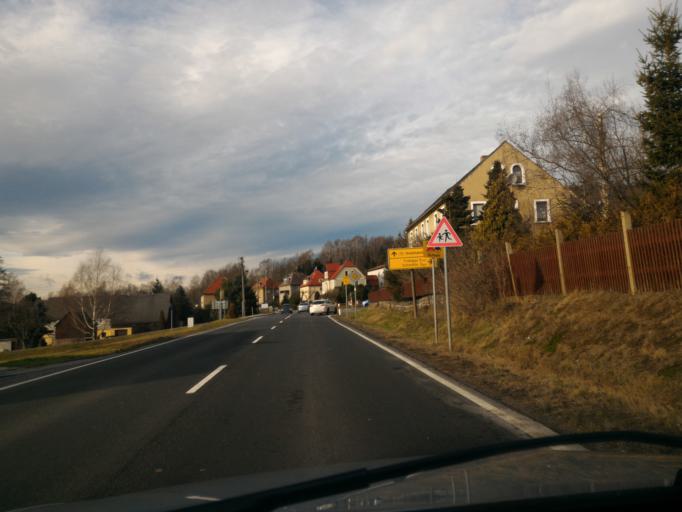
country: DE
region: Saxony
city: Demitz-Thumitz
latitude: 51.0996
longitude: 14.2418
